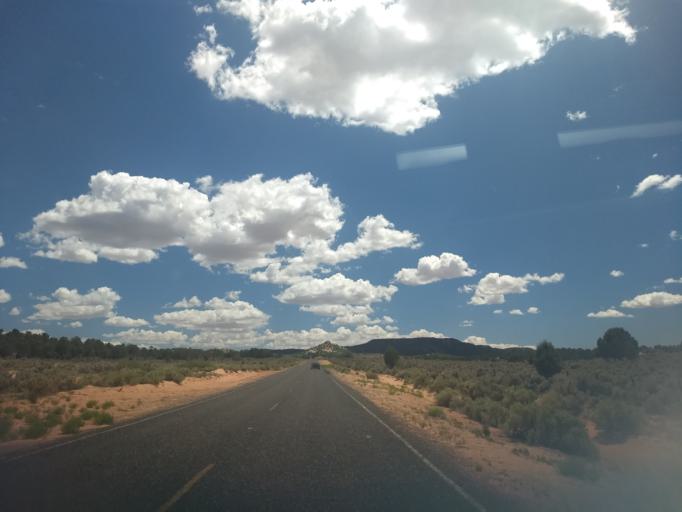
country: US
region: Utah
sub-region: Kane County
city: Kanab
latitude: 37.1532
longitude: -112.6707
